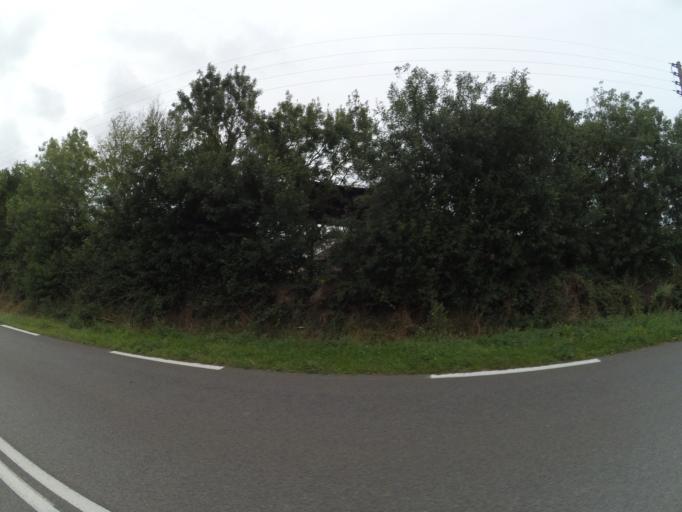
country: FR
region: Pays de la Loire
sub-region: Departement de la Vendee
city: La Garnache
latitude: 46.8578
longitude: -1.8174
